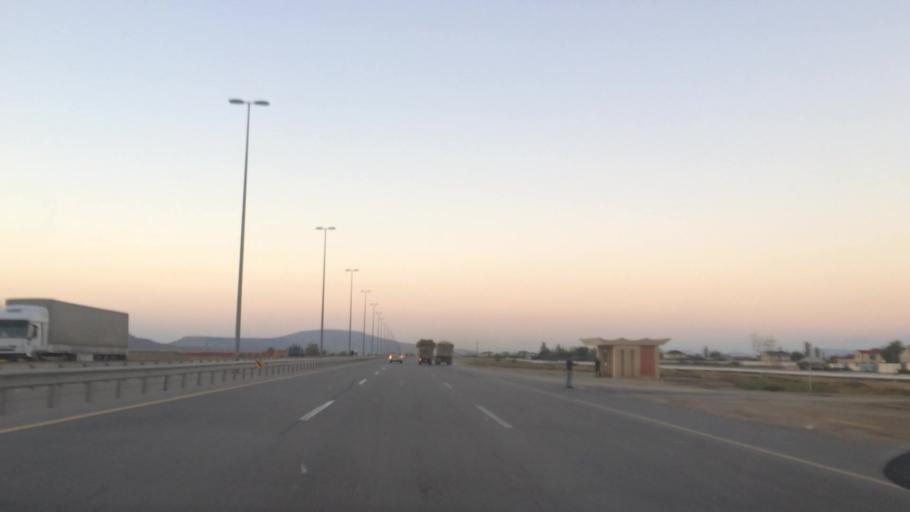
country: AZ
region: Baki
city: Qobustan
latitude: 40.0164
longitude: 49.4260
